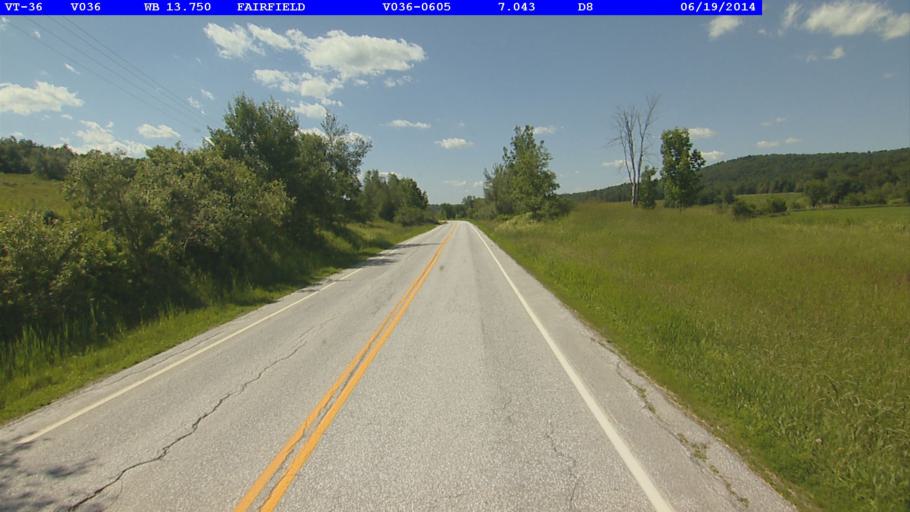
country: US
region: Vermont
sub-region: Franklin County
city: Enosburg Falls
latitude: 44.8041
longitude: -72.8968
